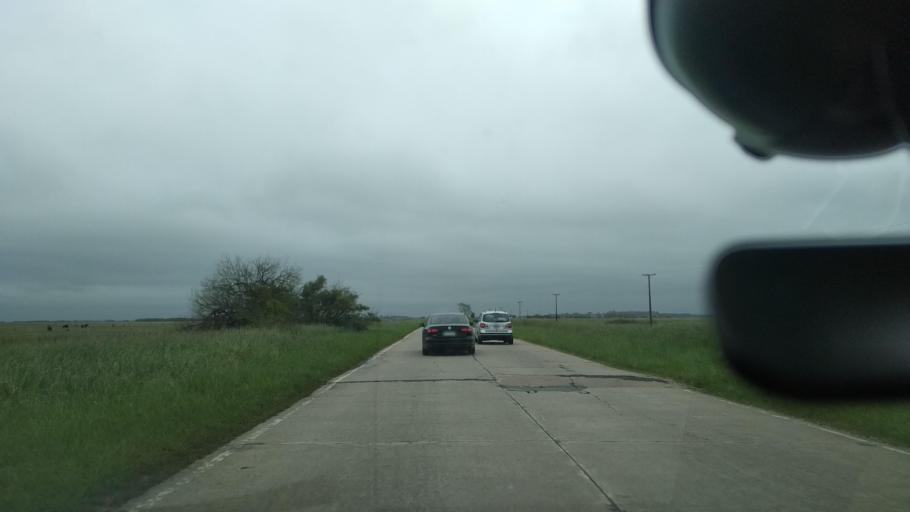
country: AR
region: Buenos Aires
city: Veronica
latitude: -35.5633
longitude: -57.2967
